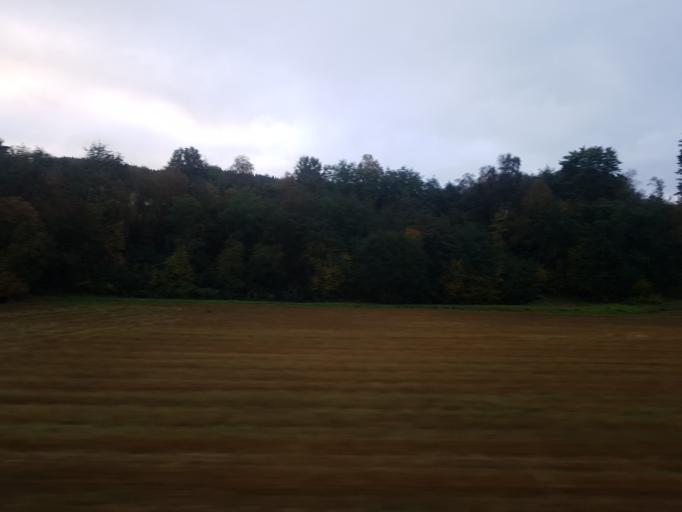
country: NO
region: Sor-Trondelag
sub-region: Melhus
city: Lundamo
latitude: 63.1507
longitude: 10.2817
